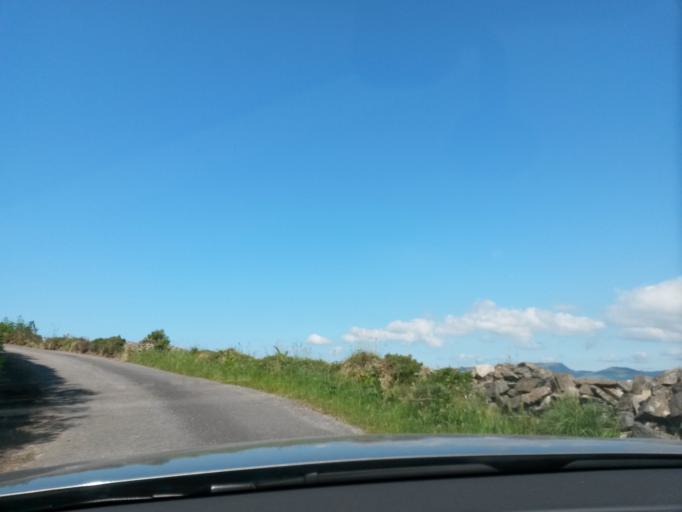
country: IE
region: Munster
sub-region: Ciarrai
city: Cahersiveen
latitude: 51.7376
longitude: -9.9443
